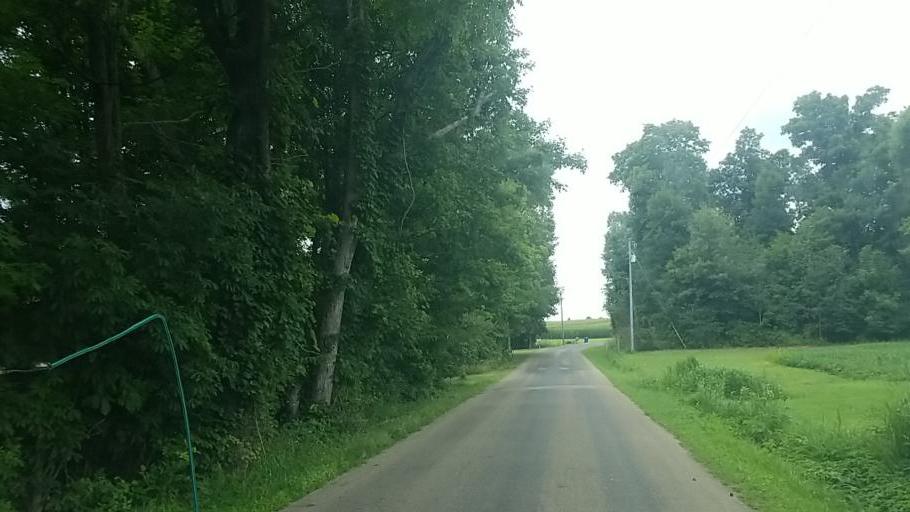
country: US
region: Ohio
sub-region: Knox County
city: Gambier
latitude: 40.3322
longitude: -82.4309
